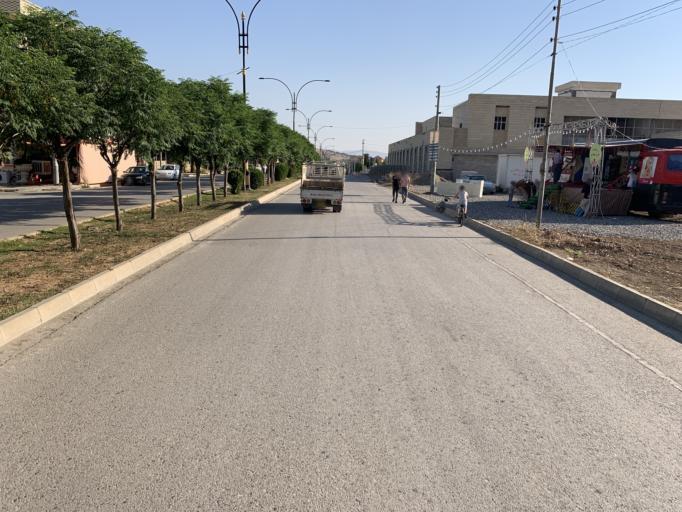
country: IQ
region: As Sulaymaniyah
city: Raniye
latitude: 36.2461
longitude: 44.8745
